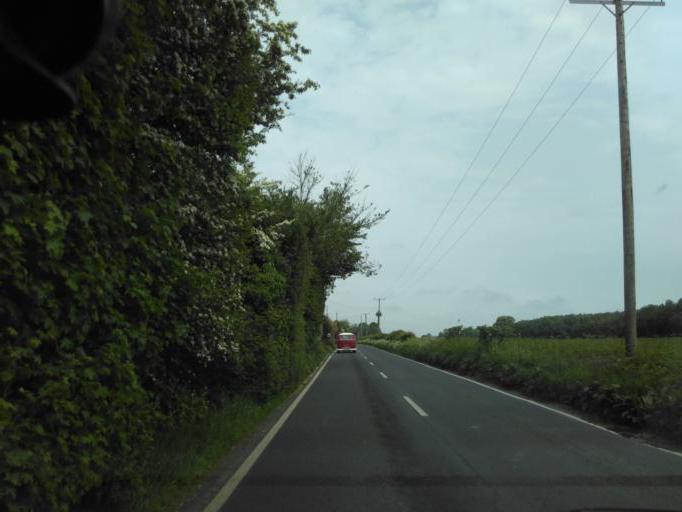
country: GB
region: England
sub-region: Kent
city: Chartham
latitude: 51.2073
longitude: 1.0586
